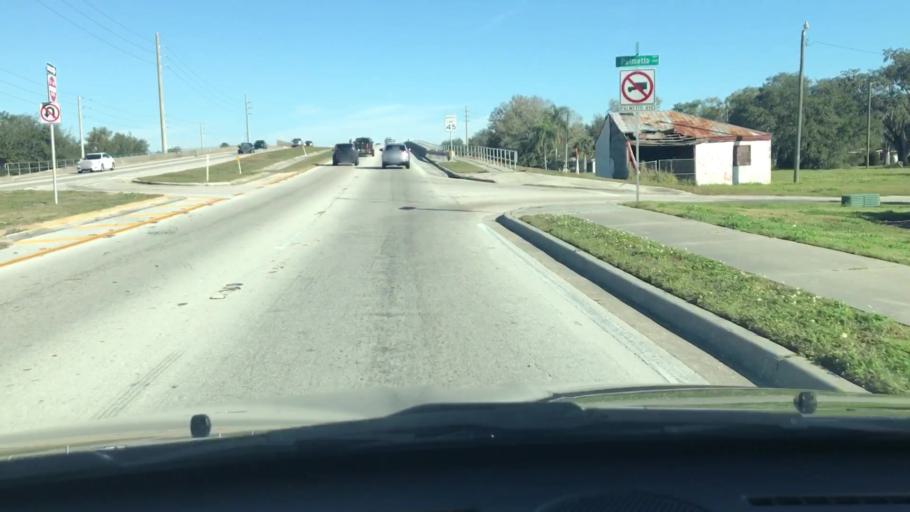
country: US
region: Florida
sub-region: Osceola County
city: Kissimmee
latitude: 28.2830
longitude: -81.4160
